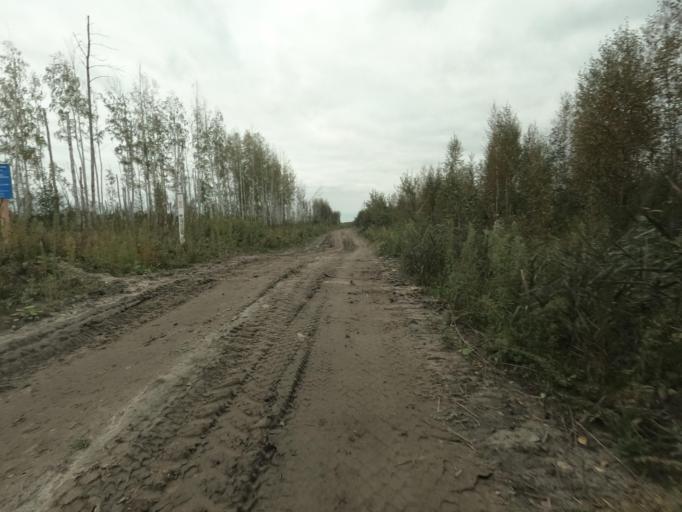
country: RU
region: St.-Petersburg
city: Sapernyy
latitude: 59.7544
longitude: 30.7029
